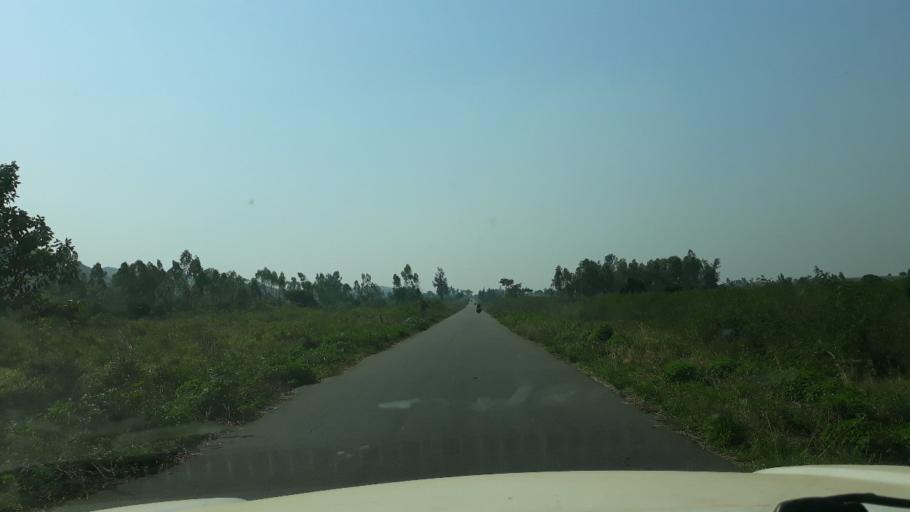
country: CD
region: South Kivu
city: Uvira
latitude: -3.2175
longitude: 29.1649
